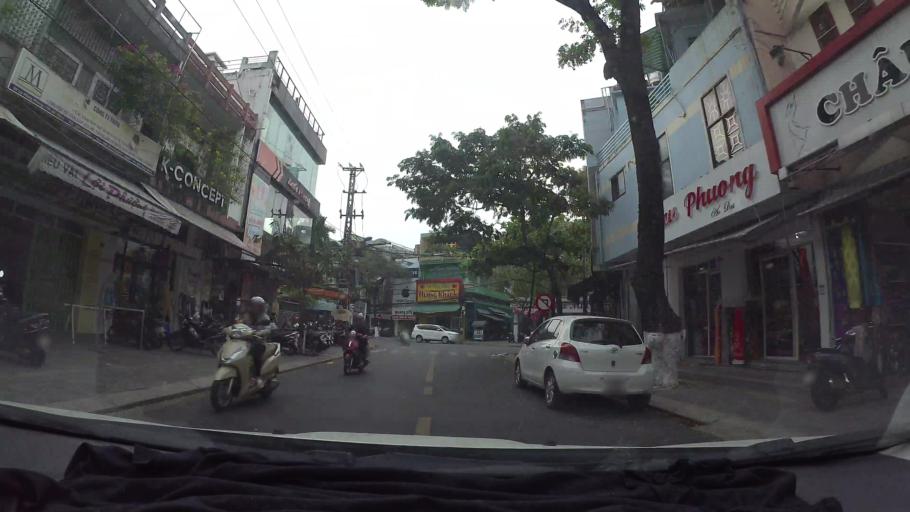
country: VN
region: Da Nang
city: Da Nang
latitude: 16.0641
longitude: 108.2191
